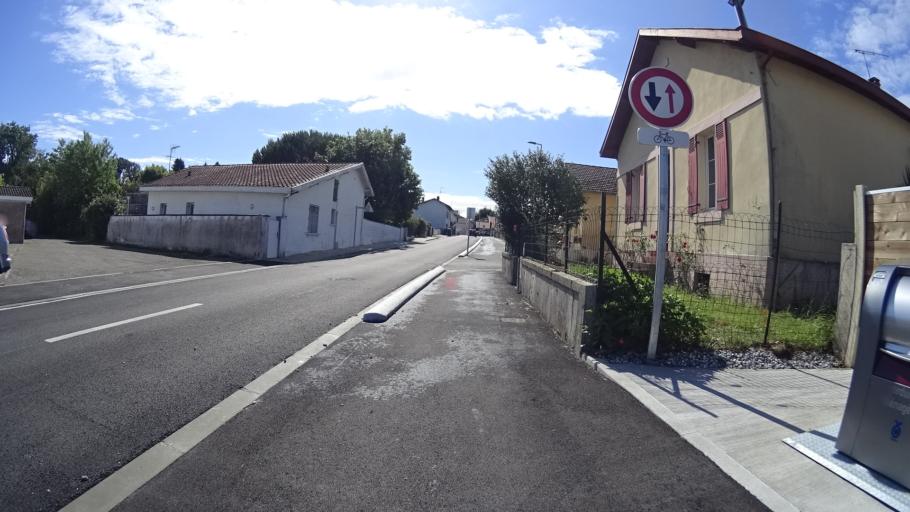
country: FR
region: Aquitaine
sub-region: Departement des Landes
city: Dax
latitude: 43.7012
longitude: -1.0659
